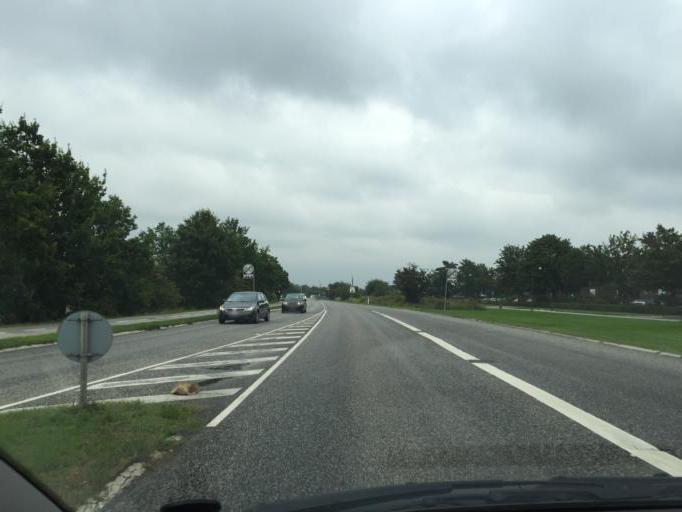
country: DK
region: Capital Region
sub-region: Herlev Kommune
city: Herlev
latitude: 55.7448
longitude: 12.4352
